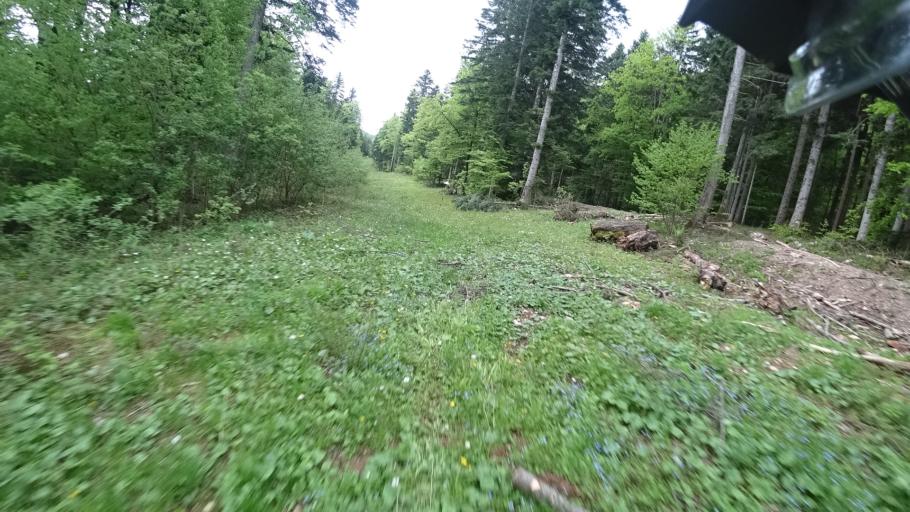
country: HR
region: Karlovacka
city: Plaski
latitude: 44.9658
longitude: 15.4033
